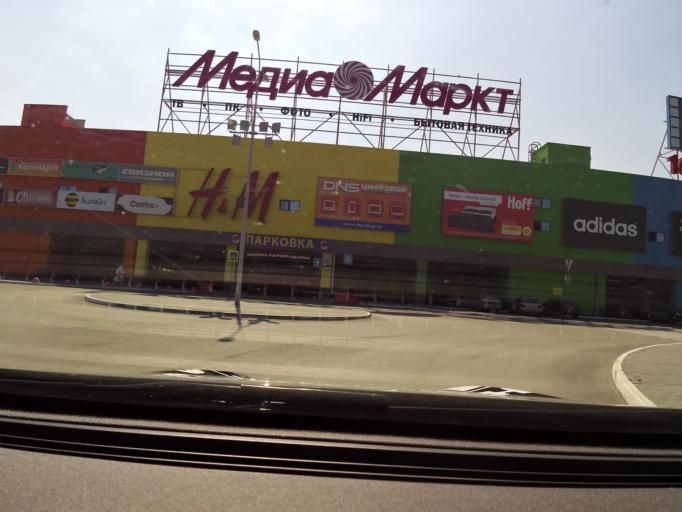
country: RU
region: Sverdlovsk
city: Shirokaya Rechka
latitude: 56.8180
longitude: 60.5368
